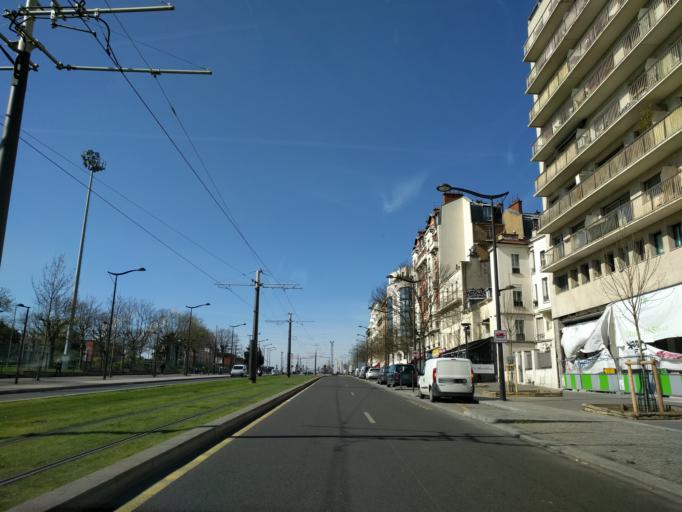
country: FR
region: Ile-de-France
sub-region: Departement du Val-de-Marne
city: Charenton-le-Pont
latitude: 48.8331
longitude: 2.4011
